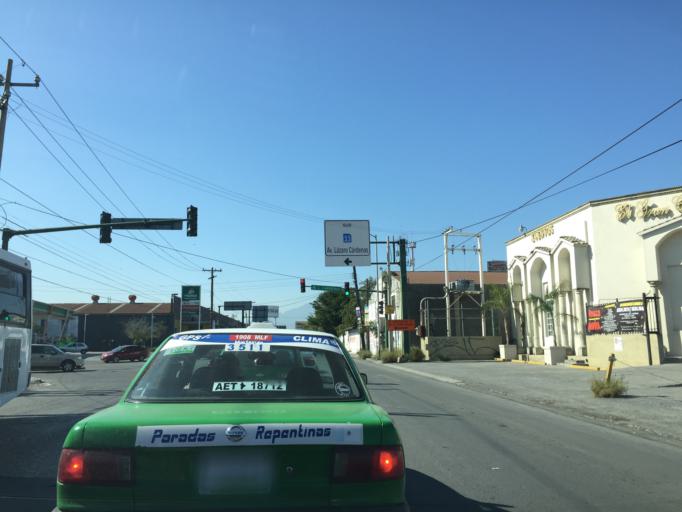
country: MX
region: Nuevo Leon
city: Guadalupe
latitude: 25.6954
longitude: -100.2299
